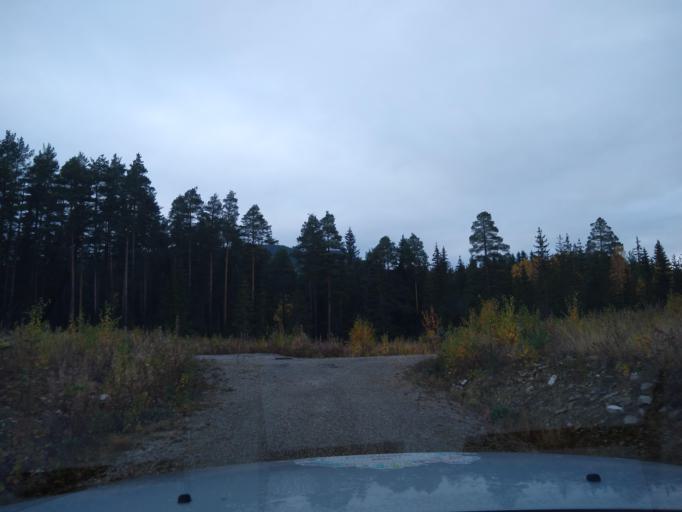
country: NO
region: Oppland
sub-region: Ringebu
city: Ringebu
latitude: 61.5347
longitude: 10.1260
